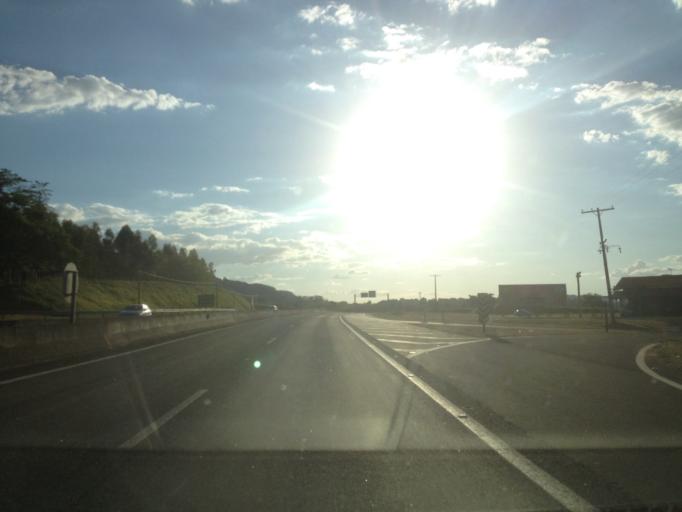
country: BR
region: Sao Paulo
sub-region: Brotas
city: Brotas
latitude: -22.2625
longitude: -48.2338
